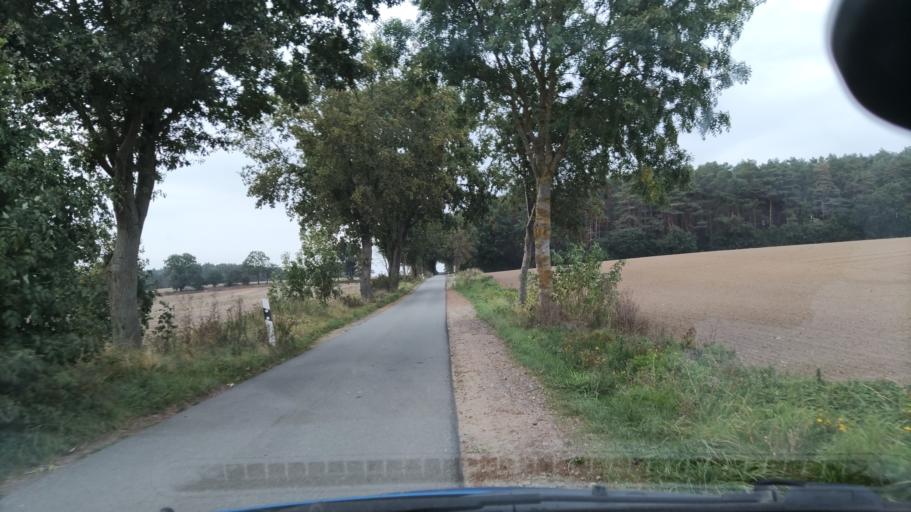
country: DE
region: Lower Saxony
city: Karwitz
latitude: 53.0975
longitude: 11.0153
